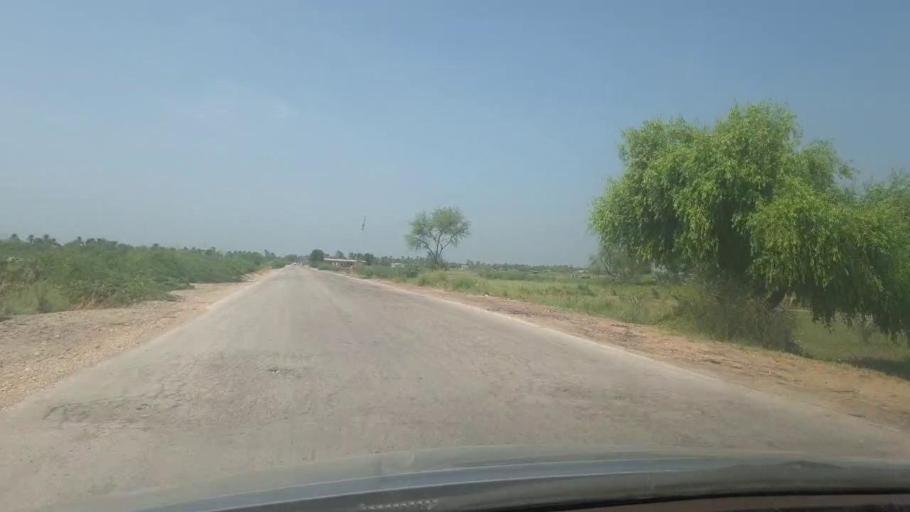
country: PK
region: Sindh
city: Ranipur
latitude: 27.2536
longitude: 68.5852
